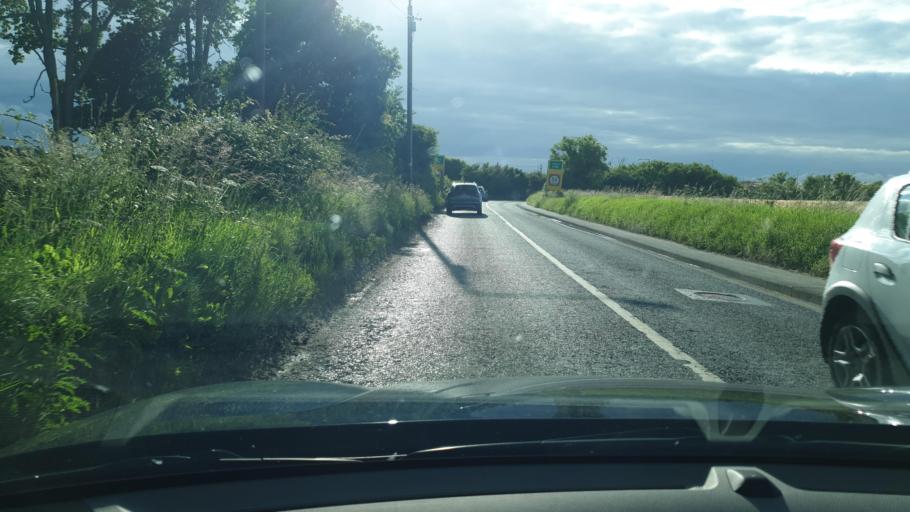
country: IE
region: Leinster
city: Lusk
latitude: 53.5226
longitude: -6.1544
